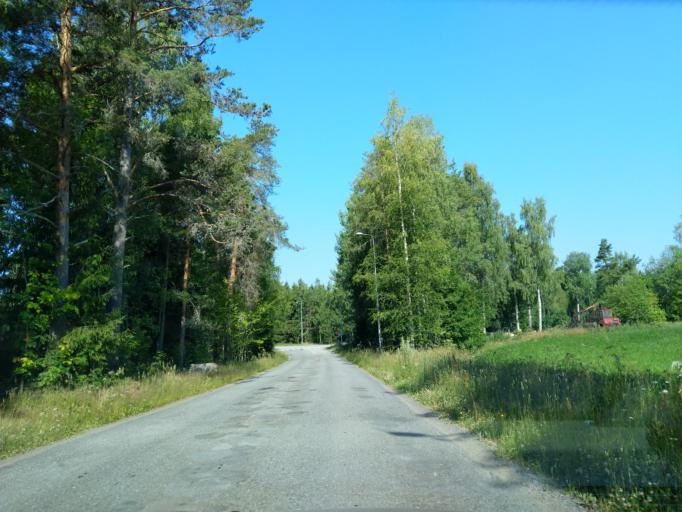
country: FI
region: Satakunta
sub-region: Pori
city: Pomarkku
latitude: 61.6890
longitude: 22.0049
